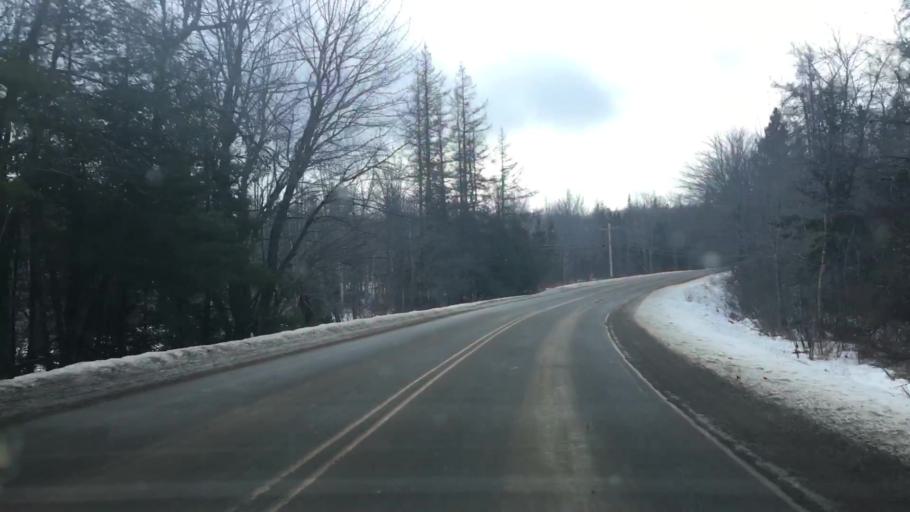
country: US
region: Maine
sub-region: Washington County
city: Calais
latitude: 45.0431
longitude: -67.3275
